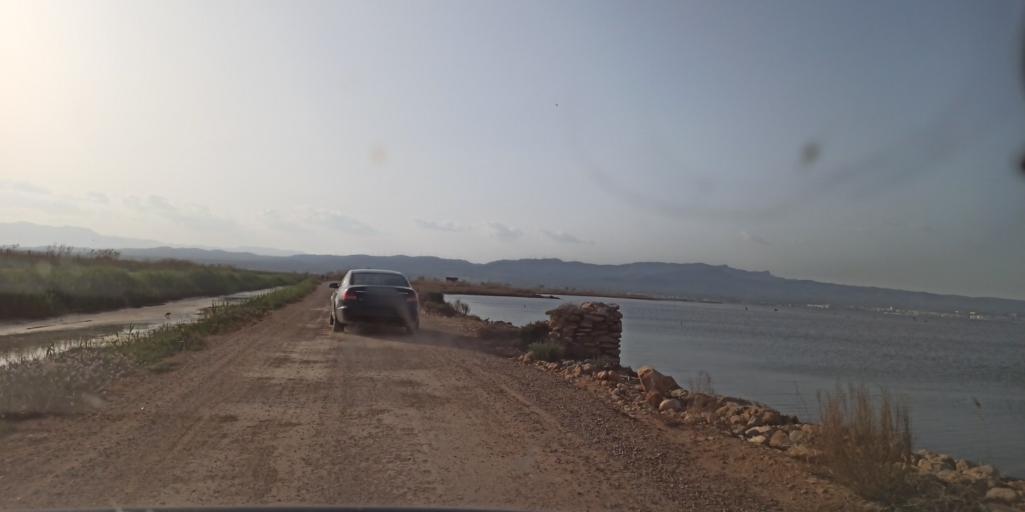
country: ES
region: Catalonia
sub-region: Provincia de Tarragona
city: L'Ampolla
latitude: 40.7689
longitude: 0.7317
